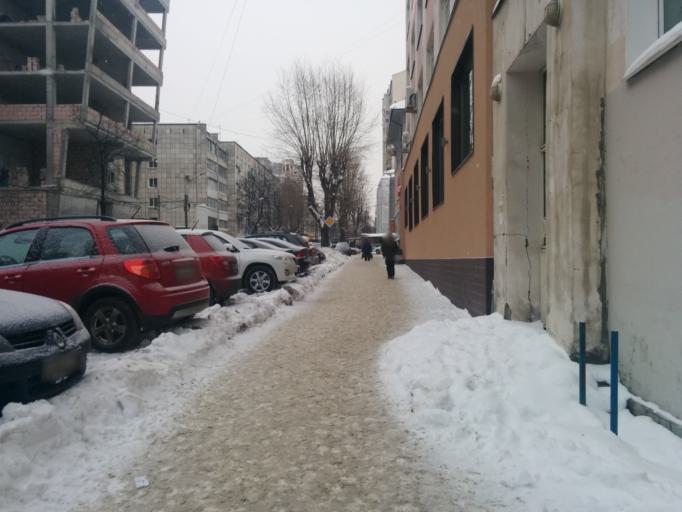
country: RU
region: Perm
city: Perm
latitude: 58.0138
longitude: 56.2495
